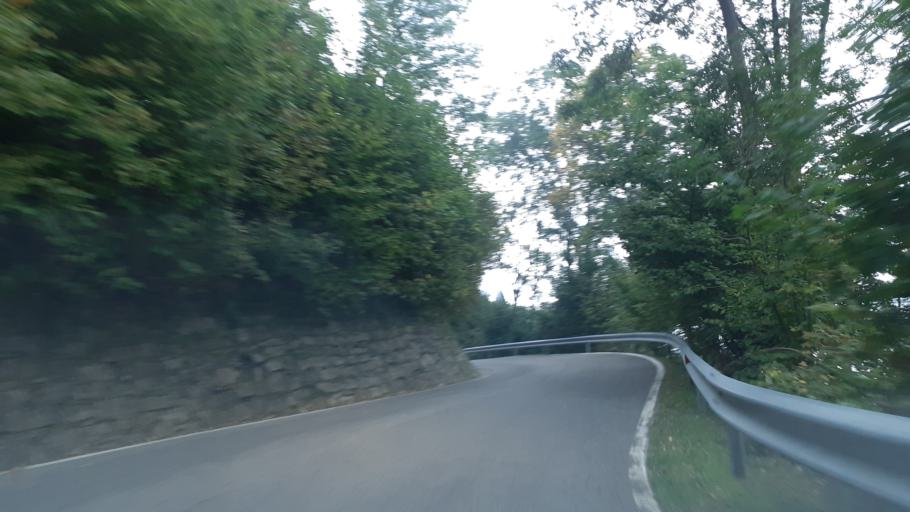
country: IT
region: Lombardy
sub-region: Provincia di Lecco
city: Ballabio
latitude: 45.9028
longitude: 9.4006
